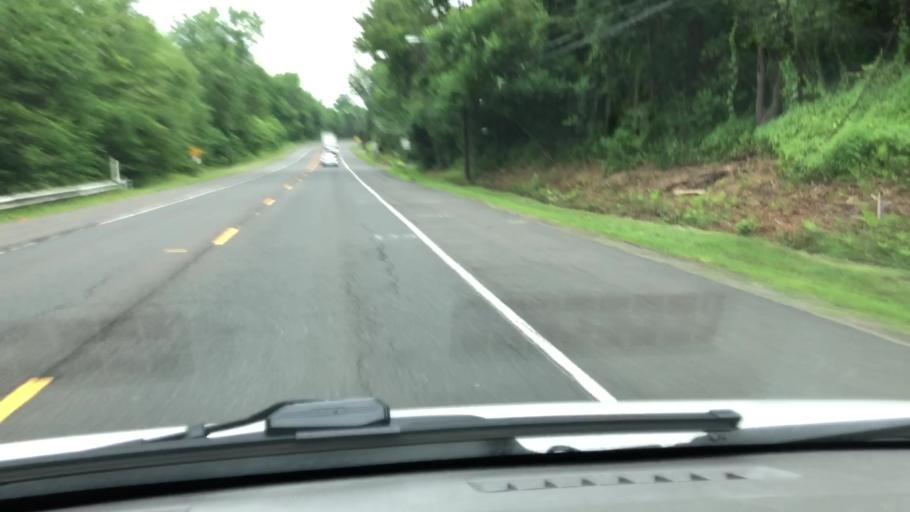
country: US
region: Massachusetts
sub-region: Berkshire County
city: Lanesborough
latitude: 42.5041
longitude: -73.1952
